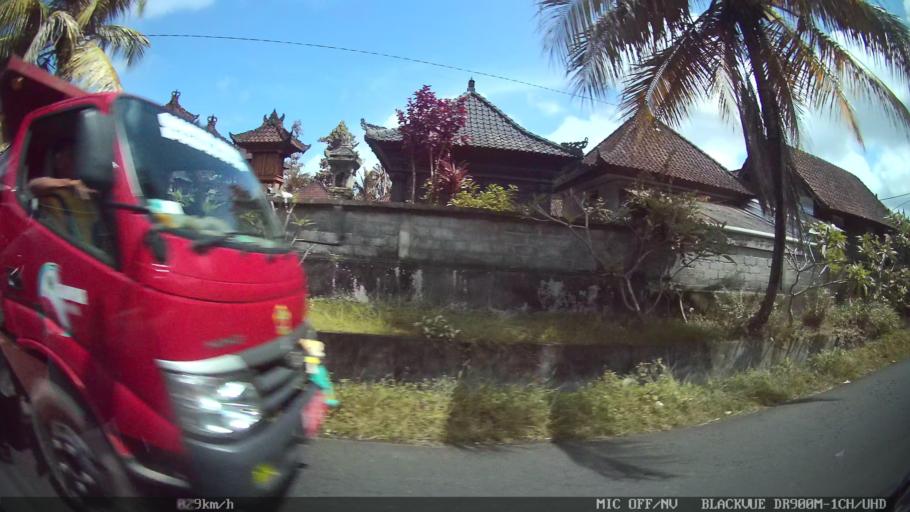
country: ID
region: Bali
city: Banjar Mulung
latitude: -8.5140
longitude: 115.3191
